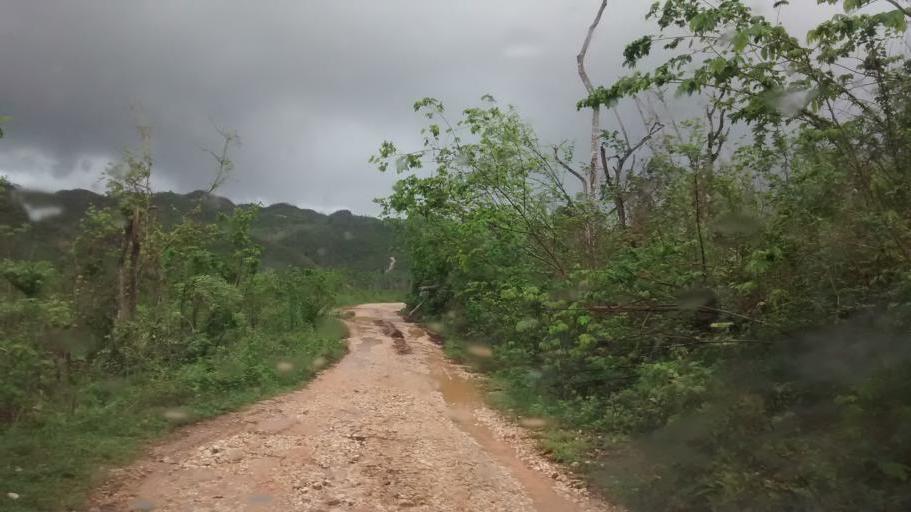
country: HT
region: Grandans
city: Corail
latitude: 18.5370
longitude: -73.9866
